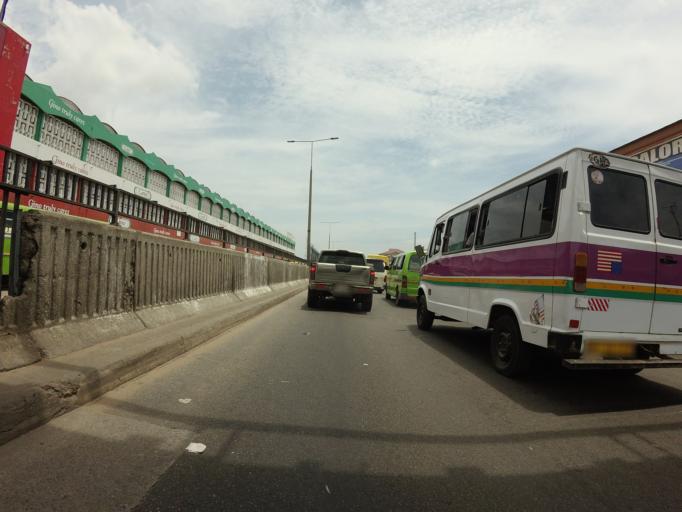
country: GH
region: Greater Accra
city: Accra
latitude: 5.5663
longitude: -0.2377
